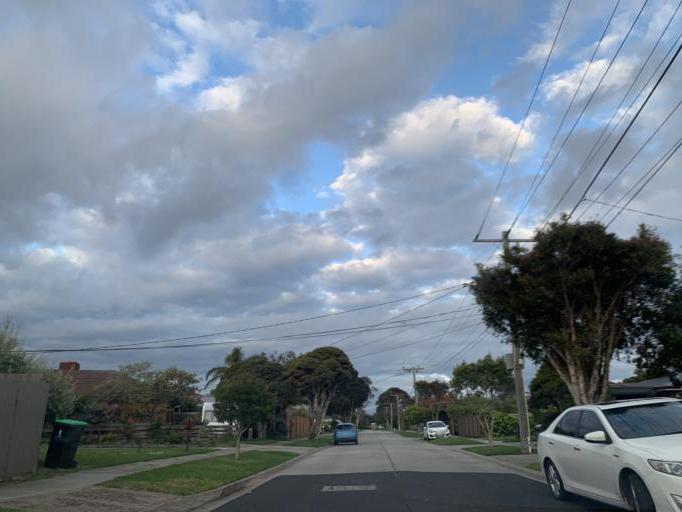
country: AU
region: Victoria
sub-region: Kingston
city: Aspendale
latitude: -38.0219
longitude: 145.1059
